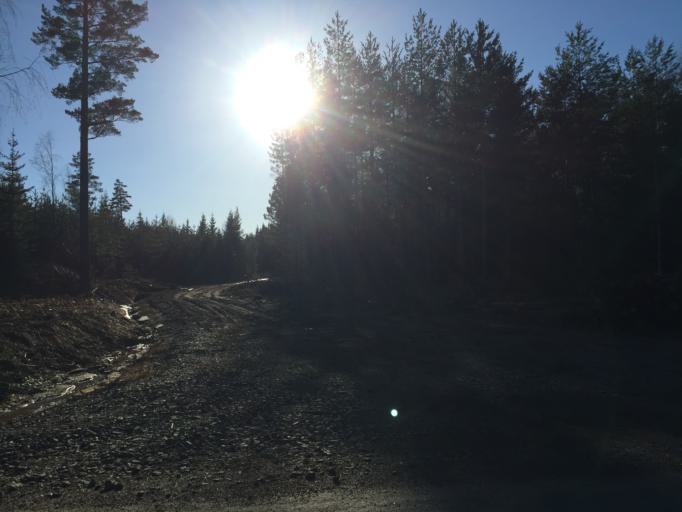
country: SE
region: Soedermanland
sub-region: Vingakers Kommun
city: Vingaker
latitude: 58.9881
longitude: 15.6684
